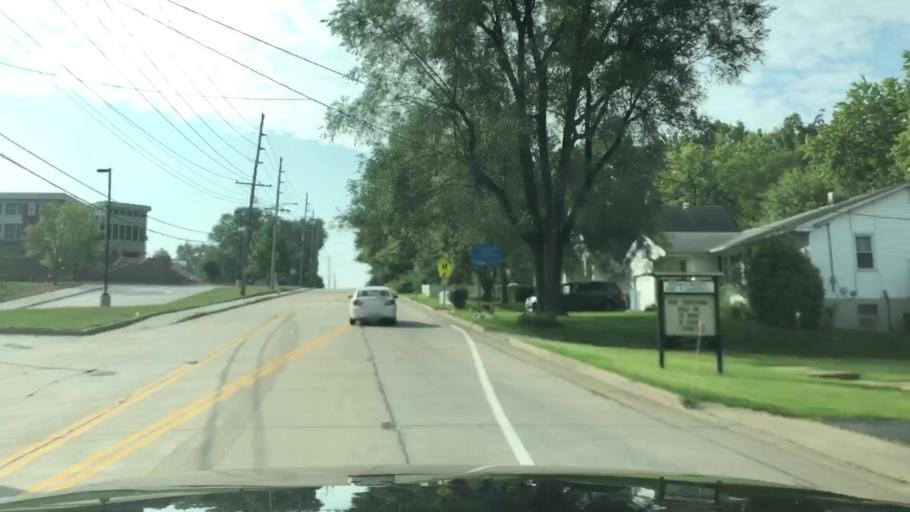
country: US
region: Missouri
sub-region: Saint Charles County
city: Saint Charles
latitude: 38.7928
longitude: -90.4977
